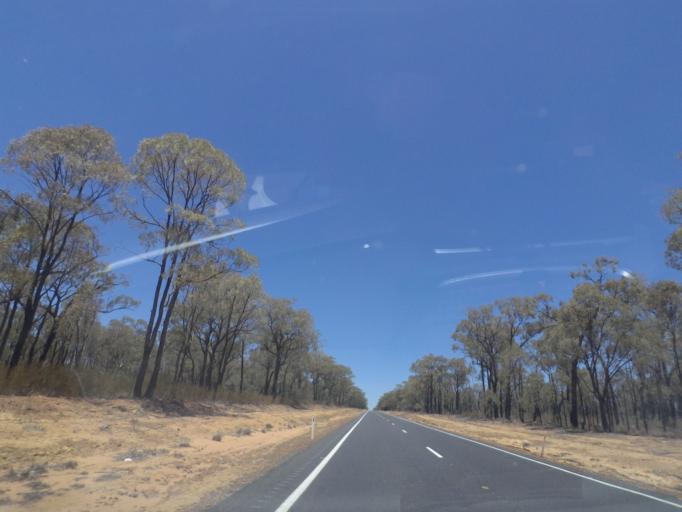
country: AU
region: New South Wales
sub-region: Narrabri
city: Narrabri
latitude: -30.7304
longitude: 149.5208
